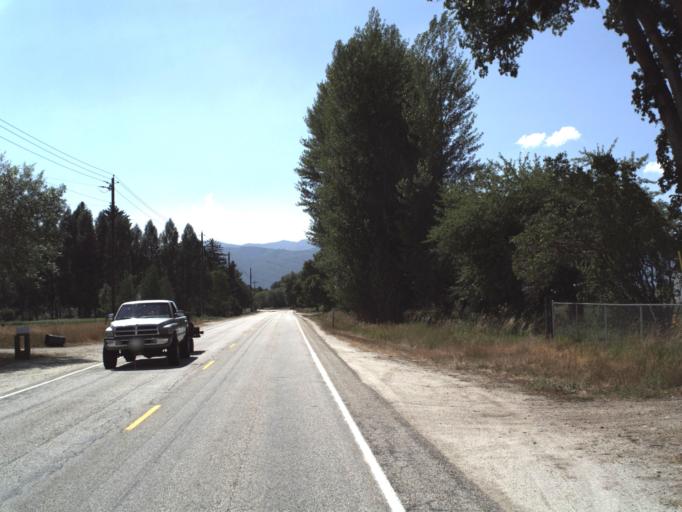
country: US
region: Utah
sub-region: Weber County
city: Wolf Creek
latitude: 41.2611
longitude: -111.7211
